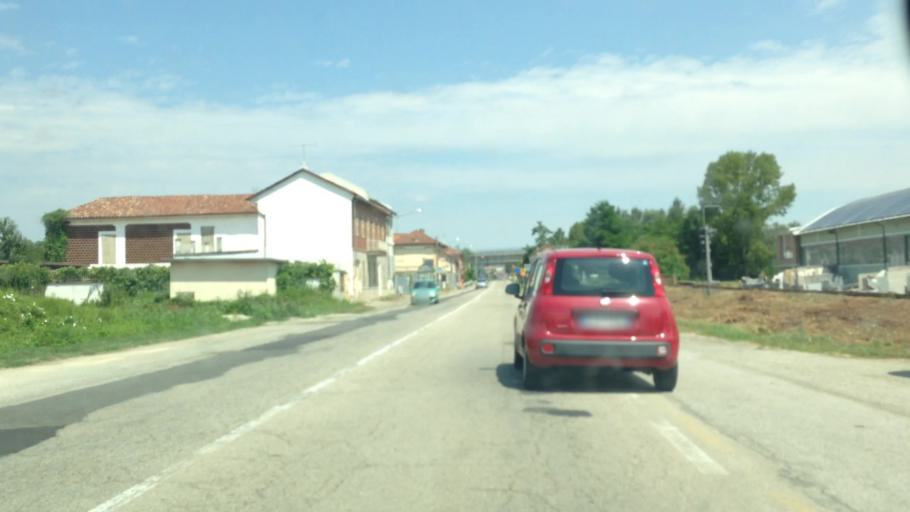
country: IT
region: Piedmont
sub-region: Provincia di Asti
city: Portacomaro
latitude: 44.9424
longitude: 8.2243
